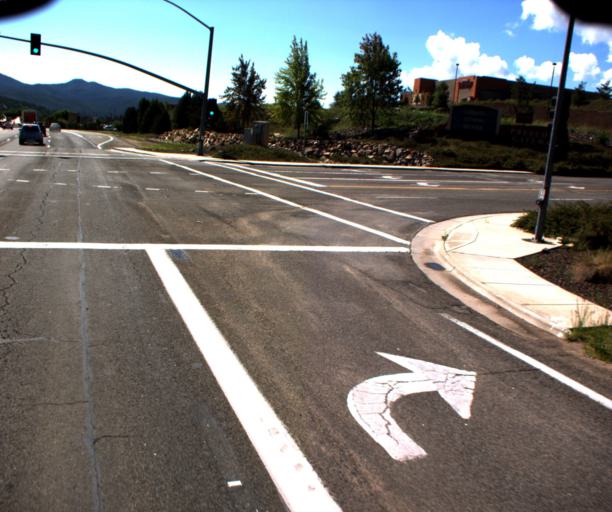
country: US
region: Arizona
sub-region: Yavapai County
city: Prescott
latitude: 34.5504
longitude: -112.4073
